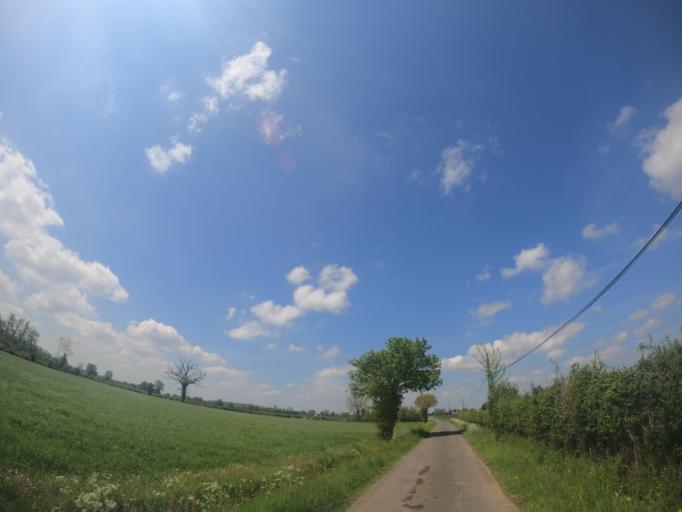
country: FR
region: Poitou-Charentes
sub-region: Departement des Deux-Sevres
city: Saint-Varent
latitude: 46.8530
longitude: -0.2335
